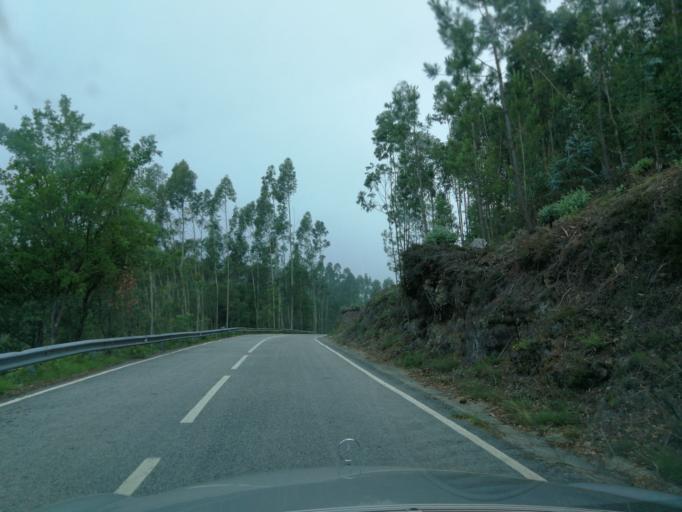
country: PT
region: Braga
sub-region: Braga
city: Braga
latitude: 41.5181
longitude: -8.3789
